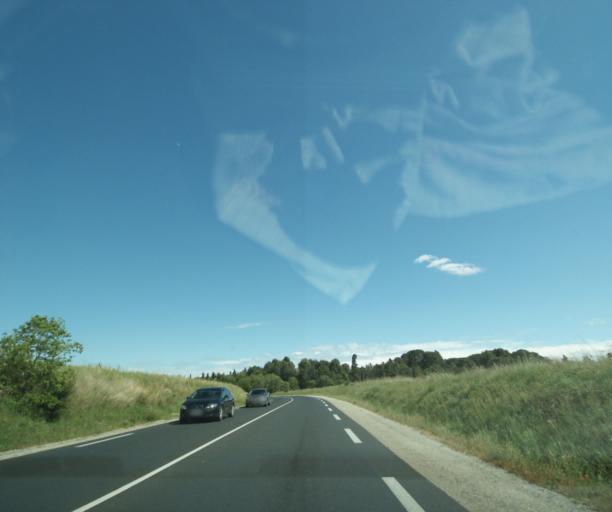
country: FR
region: Languedoc-Roussillon
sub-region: Departement de l'Herault
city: Saint-Jean-de-Vedas
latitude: 43.5873
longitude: 3.8270
